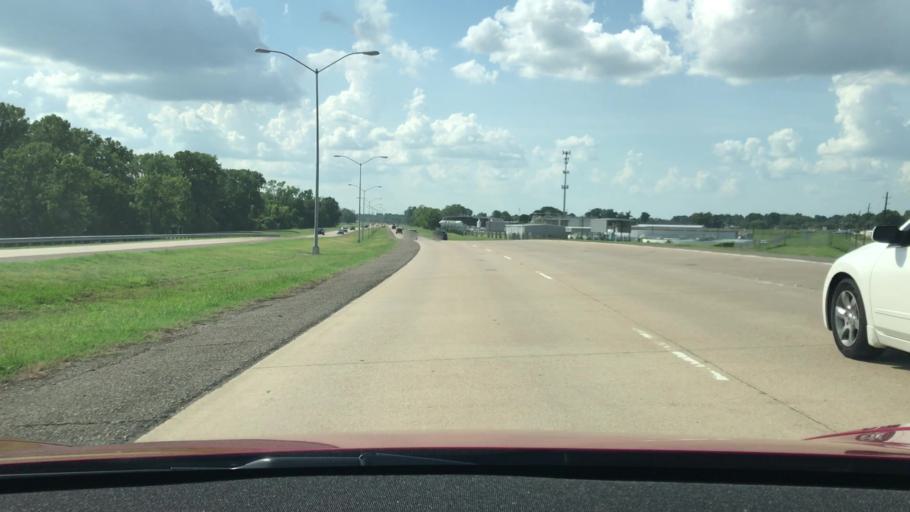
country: US
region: Louisiana
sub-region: Bossier Parish
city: Bossier City
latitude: 32.4785
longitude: -93.6804
